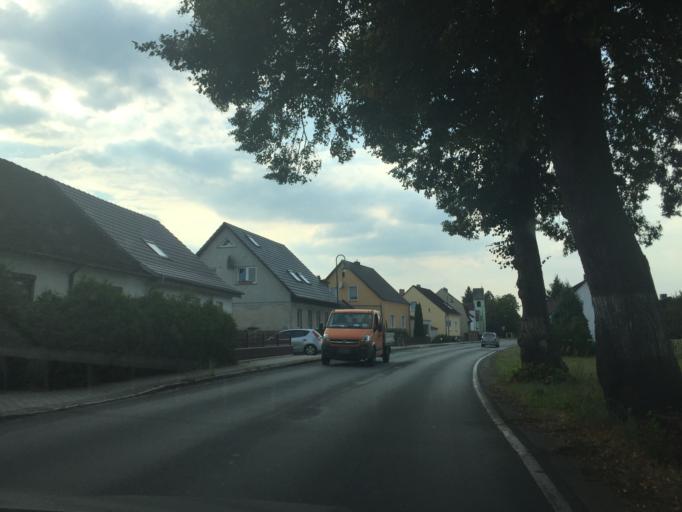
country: DE
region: Brandenburg
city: Spreenhagen
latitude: 52.3572
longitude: 13.8466
